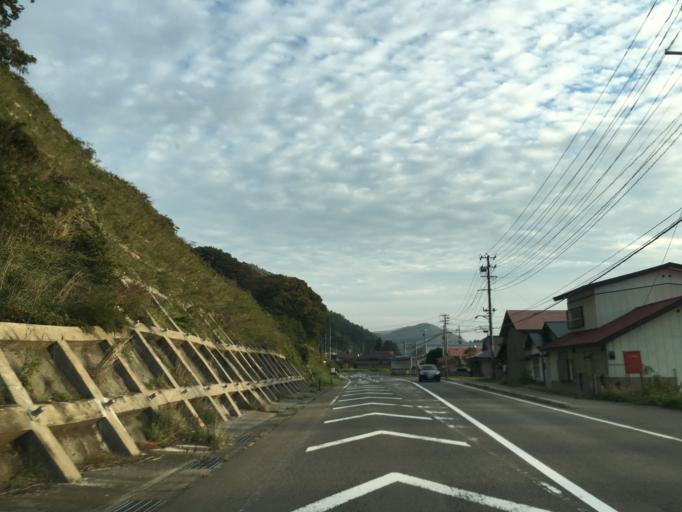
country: JP
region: Fukushima
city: Inawashiro
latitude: 37.5150
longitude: 140.1445
